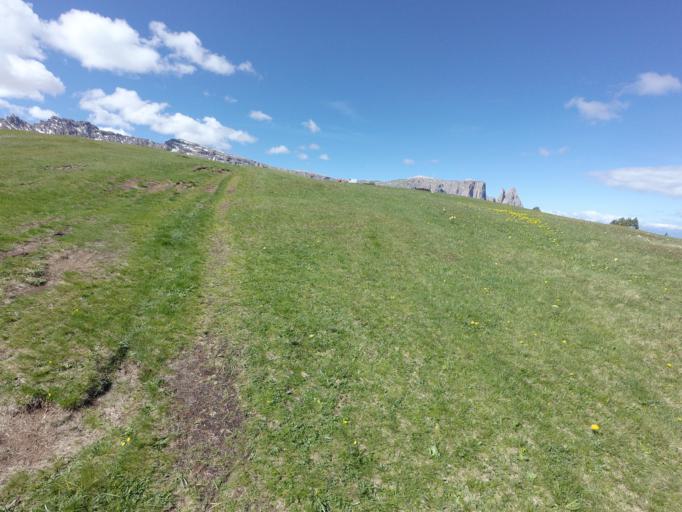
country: IT
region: Trentino-Alto Adige
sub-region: Bolzano
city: Ortisei
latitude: 46.5354
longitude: 11.6367
